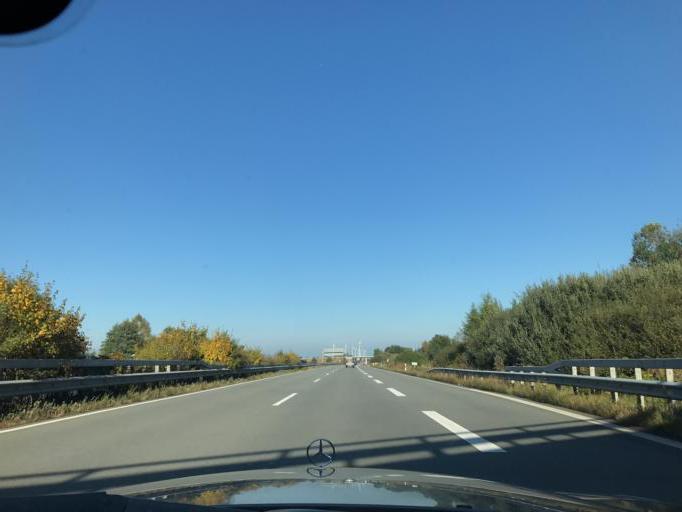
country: DE
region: Lower Saxony
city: Bunde
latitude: 53.1627
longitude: 7.2831
